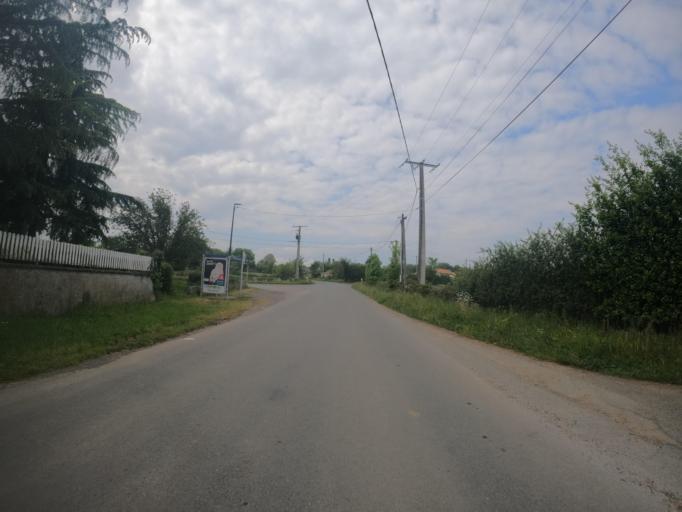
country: FR
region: Poitou-Charentes
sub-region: Departement des Deux-Sevres
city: Saint-Varent
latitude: 46.8622
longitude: -0.2718
